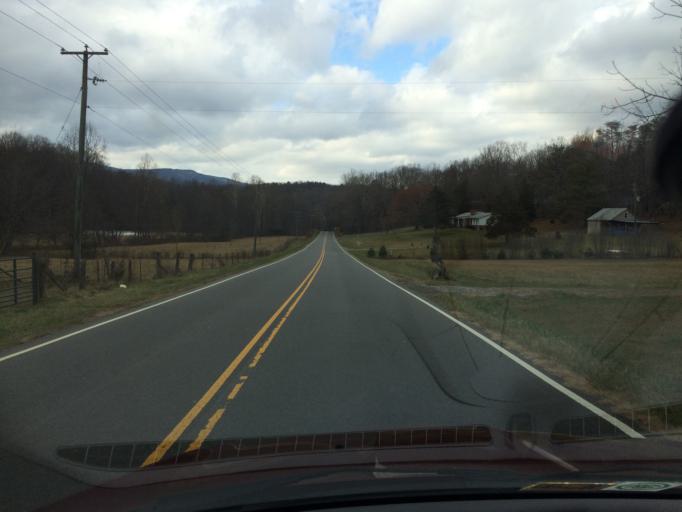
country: US
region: Virginia
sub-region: Patrick County
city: Stuart
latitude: 36.7477
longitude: -80.2645
